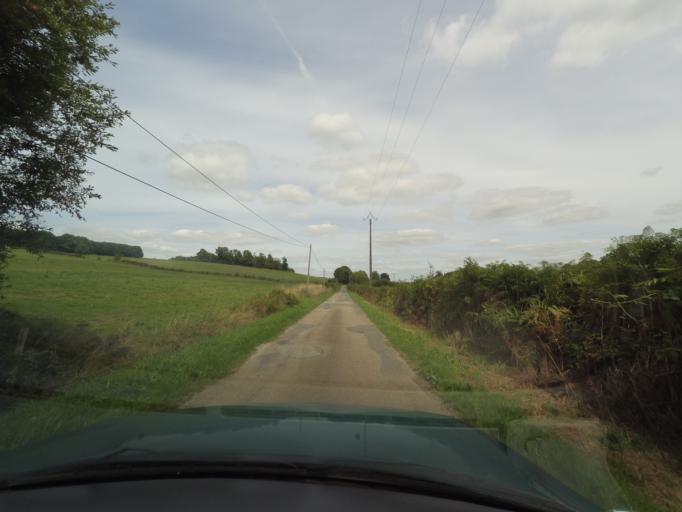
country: FR
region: Limousin
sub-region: Departement de la Haute-Vienne
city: Ladignac-le-Long
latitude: 45.6403
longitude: 1.1135
